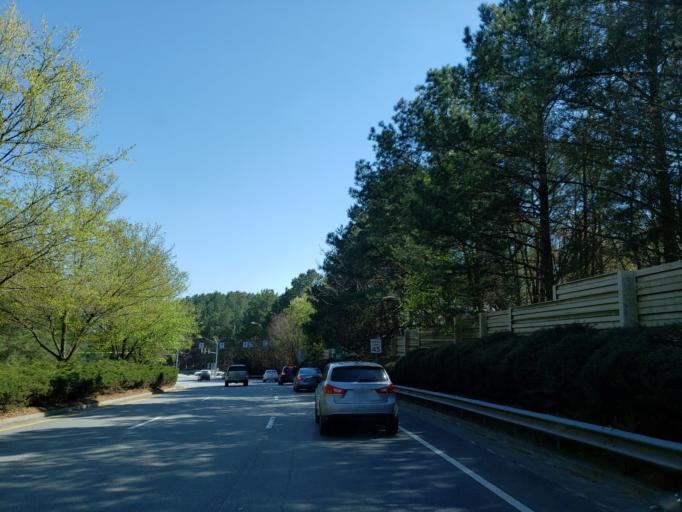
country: US
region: Georgia
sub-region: Fulton County
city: Sandy Springs
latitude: 33.9050
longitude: -84.3616
